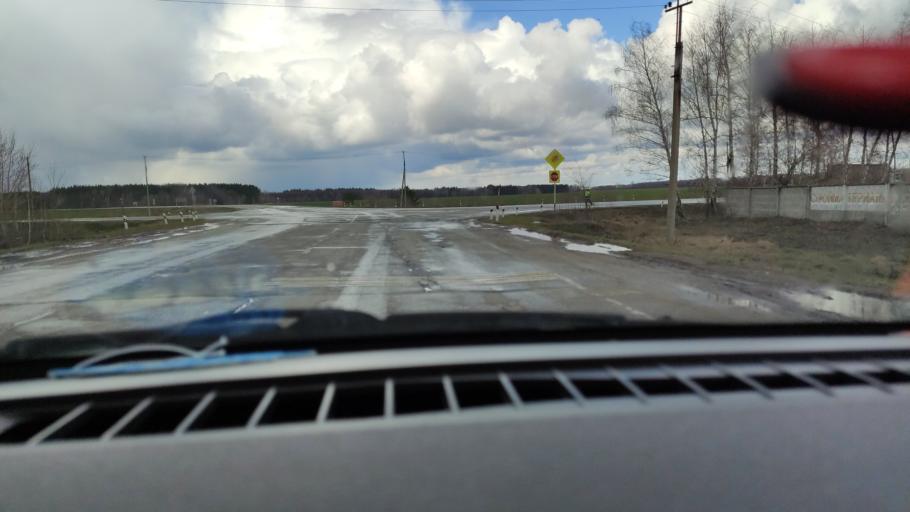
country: RU
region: Samara
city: Povolzhskiy
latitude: 53.8065
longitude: 49.7947
